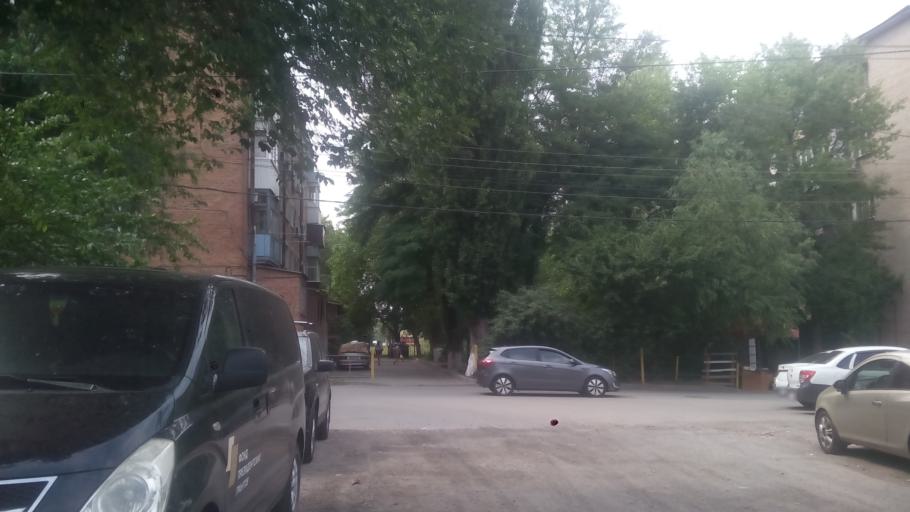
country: RU
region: Rostov
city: Rostov-na-Donu
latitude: 47.2164
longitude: 39.6589
